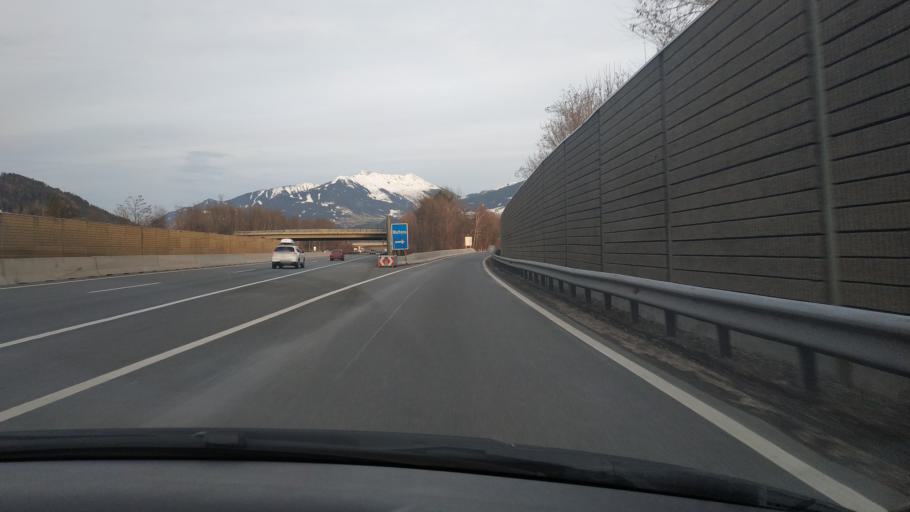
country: AT
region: Tyrol
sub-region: Politischer Bezirk Innsbruck Land
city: Fritzens
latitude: 47.2993
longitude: 11.5802
